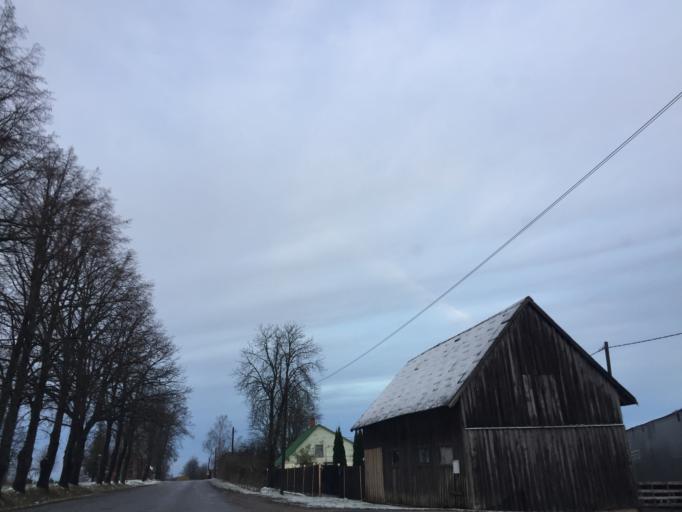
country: LV
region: Limbazu Rajons
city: Limbazi
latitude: 57.5952
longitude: 24.8510
